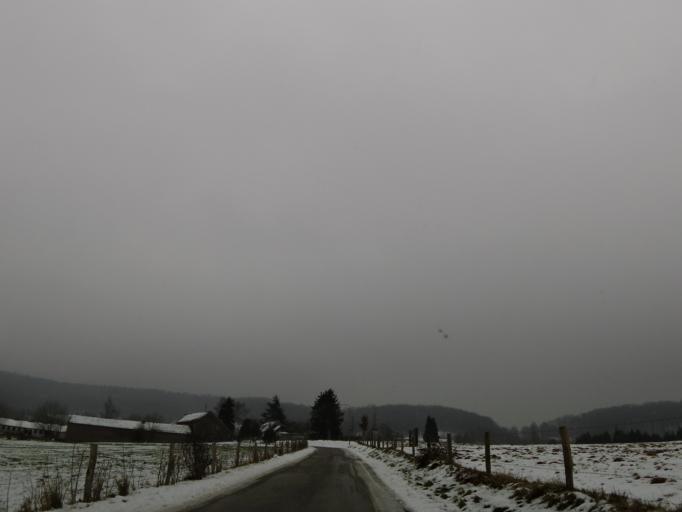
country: NL
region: Limburg
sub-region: Gemeente Vaals
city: Vaals
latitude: 50.7622
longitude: 6.0012
